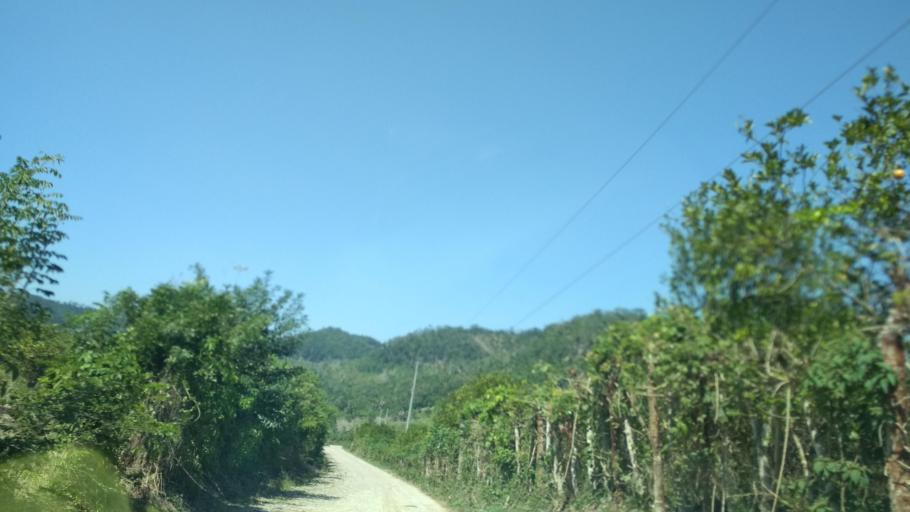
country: MX
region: Veracruz
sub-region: Papantla
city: Polutla
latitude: 20.4778
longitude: -97.2204
